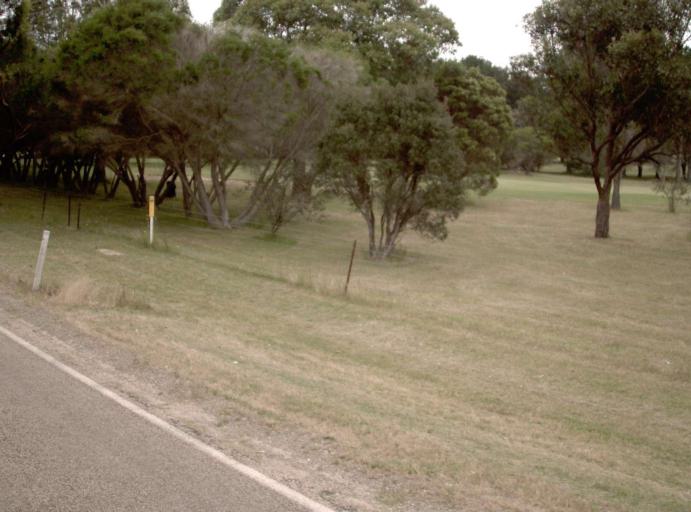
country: AU
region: Victoria
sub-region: East Gippsland
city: Bairnsdale
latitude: -37.8345
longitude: 147.4326
